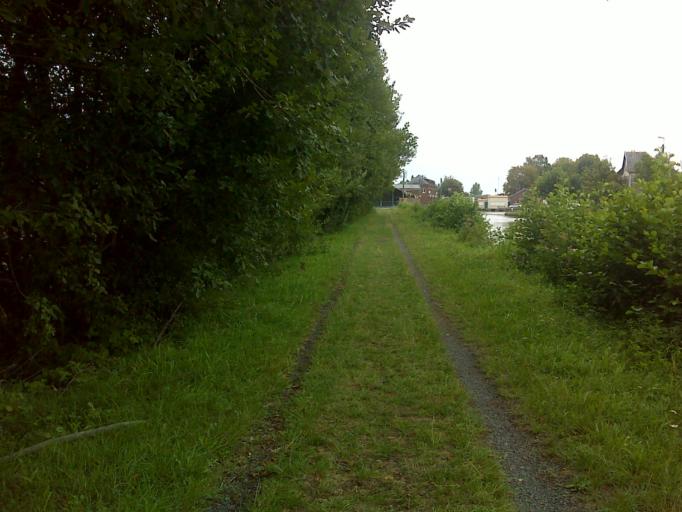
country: FR
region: Nord-Pas-de-Calais
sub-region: Departement du Nord
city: Landrecies
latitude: 50.1250
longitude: 3.6851
